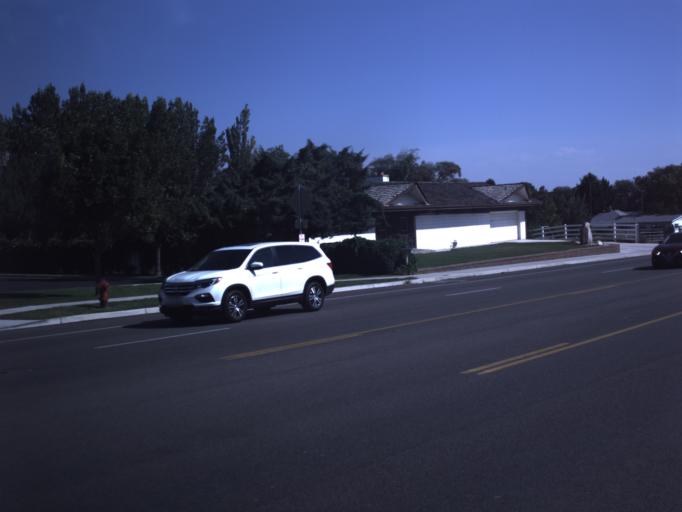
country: US
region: Utah
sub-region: Utah County
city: American Fork
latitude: 40.3848
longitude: -111.7692
